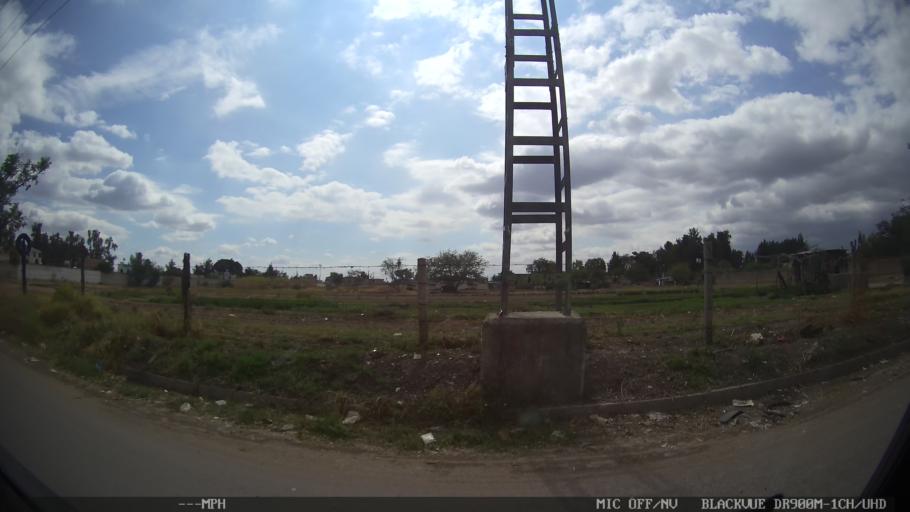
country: MX
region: Jalisco
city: Tonala
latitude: 20.6635
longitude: -103.2475
